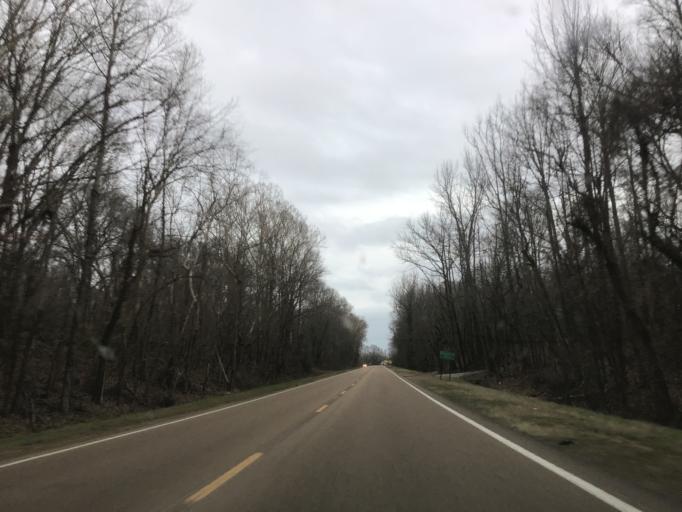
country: US
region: Mississippi
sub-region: Warren County
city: Beechwood
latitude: 32.3013
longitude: -90.7996
